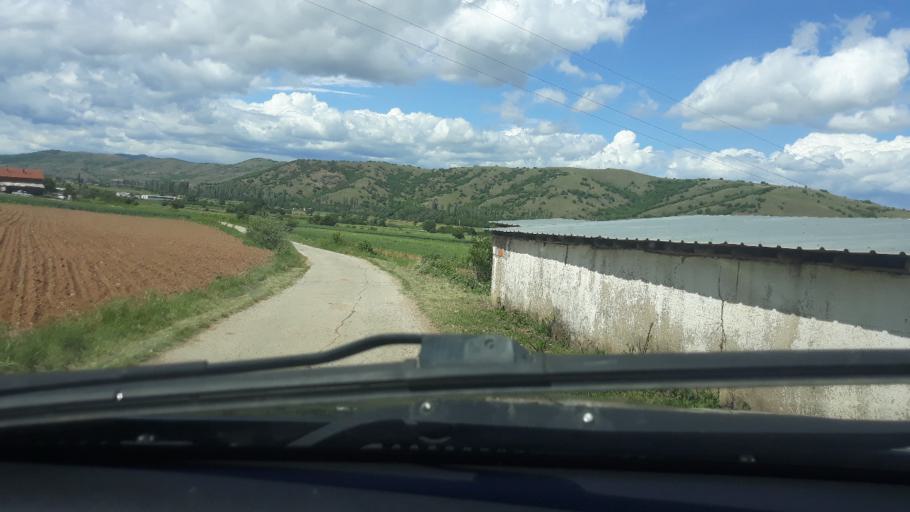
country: MK
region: Krivogastani
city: Krivogashtani
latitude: 41.3379
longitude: 21.3006
